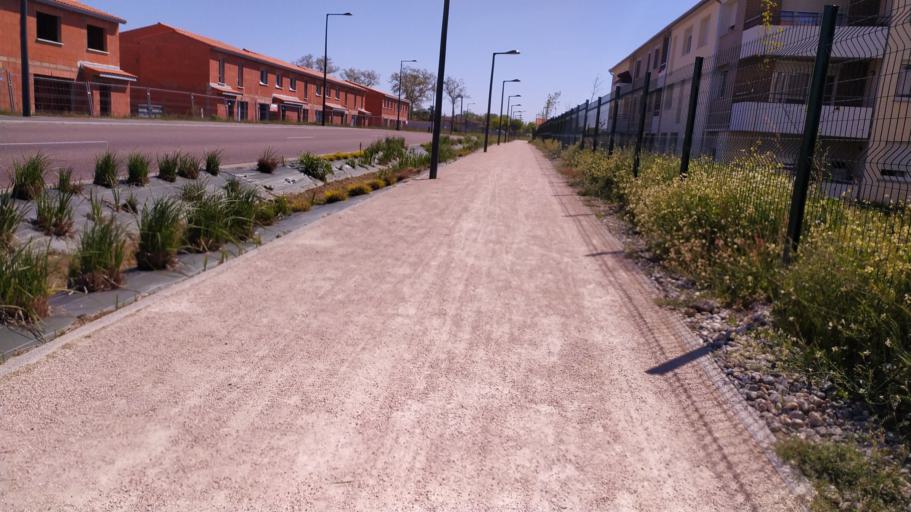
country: FR
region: Midi-Pyrenees
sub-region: Departement de la Haute-Garonne
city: Plaisance-du-Touch
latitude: 43.5718
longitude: 1.3083
